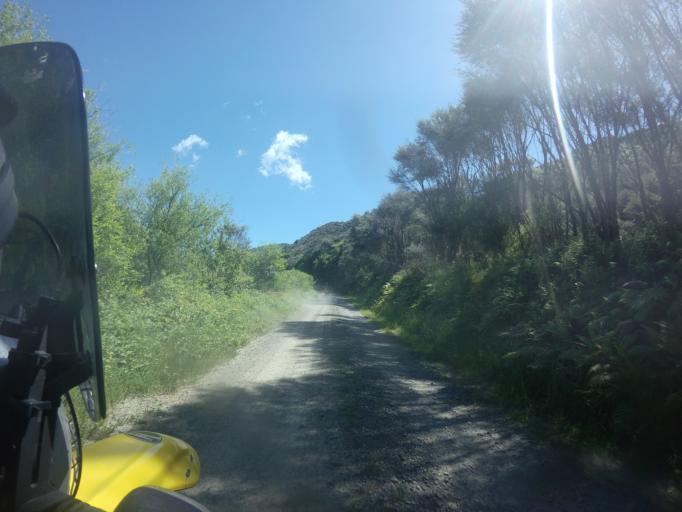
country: NZ
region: Bay of Plenty
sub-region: Opotiki District
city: Opotiki
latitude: -38.3027
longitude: 177.3322
